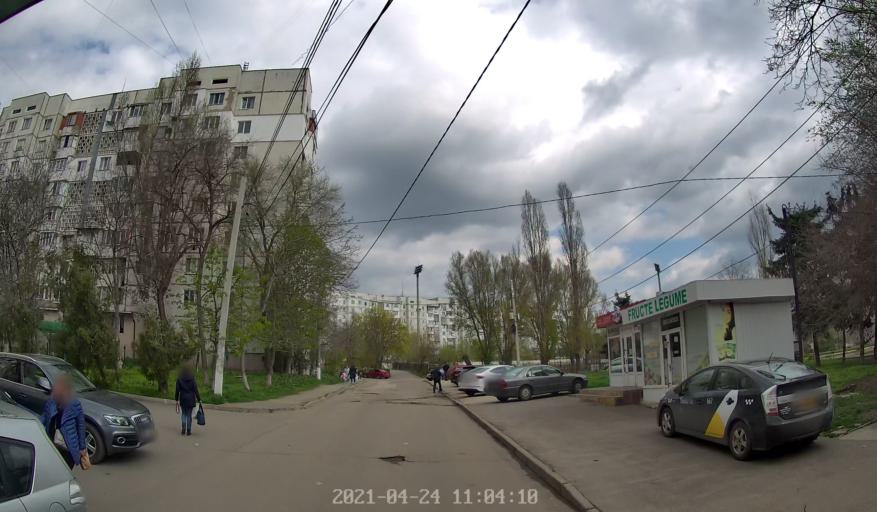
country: MD
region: Chisinau
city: Chisinau
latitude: 47.0405
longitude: 28.8849
